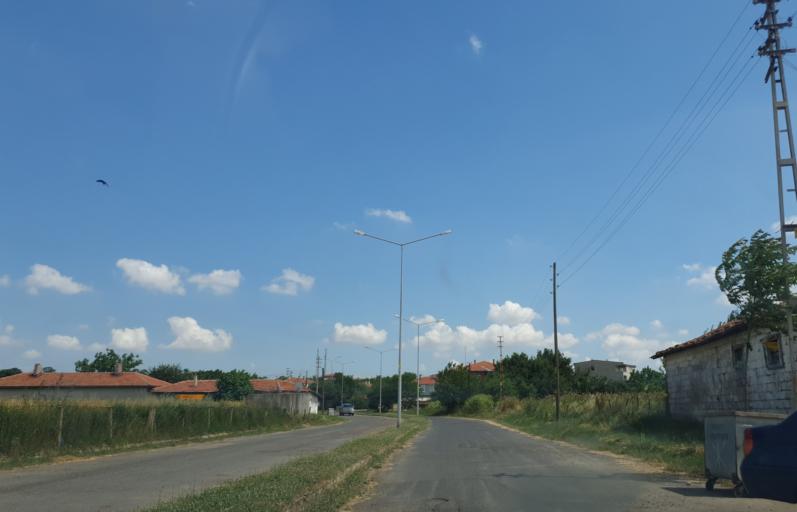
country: TR
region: Tekirdag
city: Muratli
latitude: 41.2182
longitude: 27.5443
